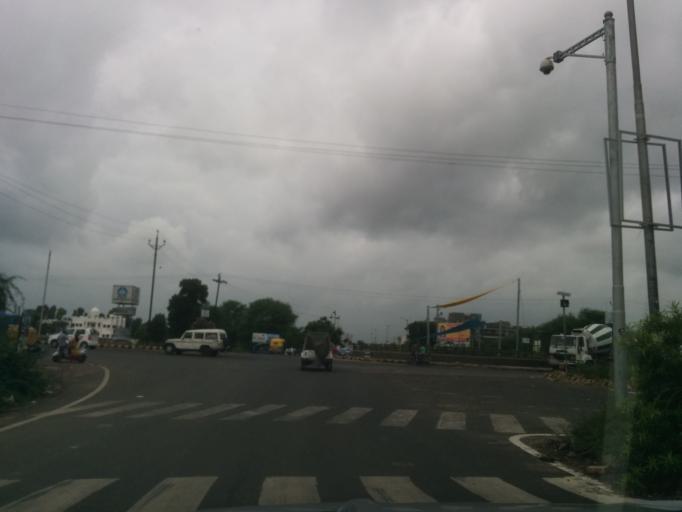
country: IN
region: Gujarat
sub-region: Ahmadabad
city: Sarkhej
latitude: 23.0530
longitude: 72.4806
